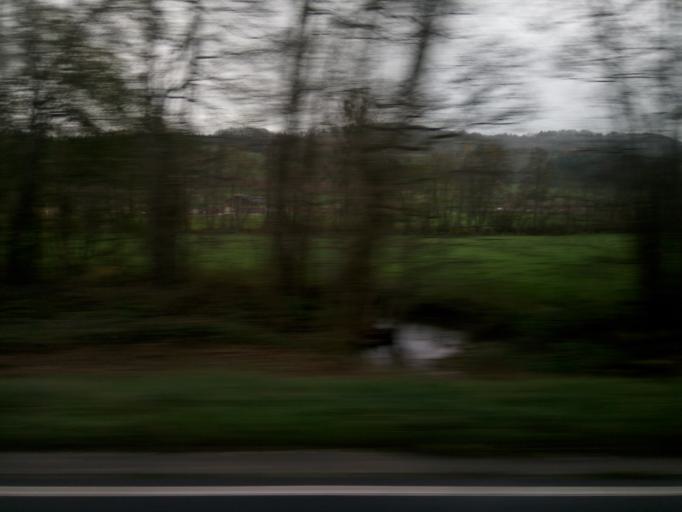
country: LU
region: Diekirch
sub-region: Canton de Vianden
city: Tandel
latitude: 49.8851
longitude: 6.1846
